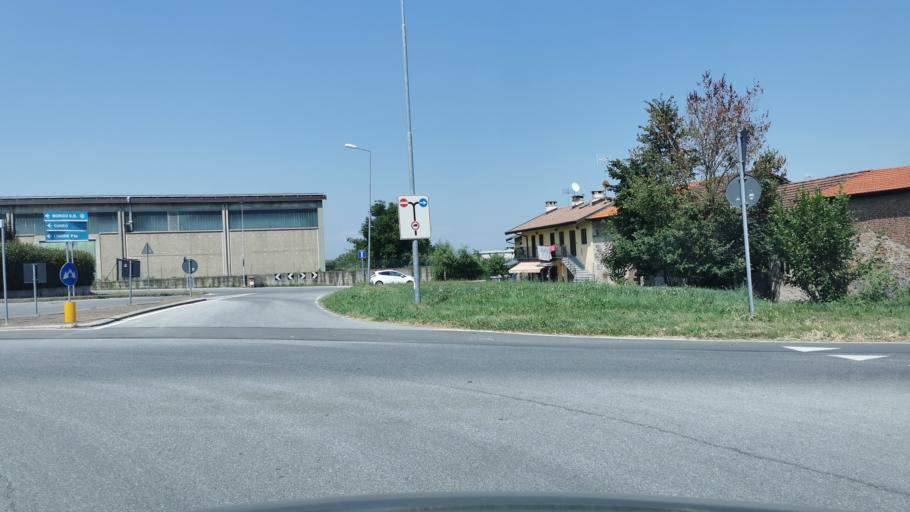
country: IT
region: Piedmont
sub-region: Provincia di Cuneo
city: Borgo San Dalmazzo
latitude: 44.3345
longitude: 7.5025
